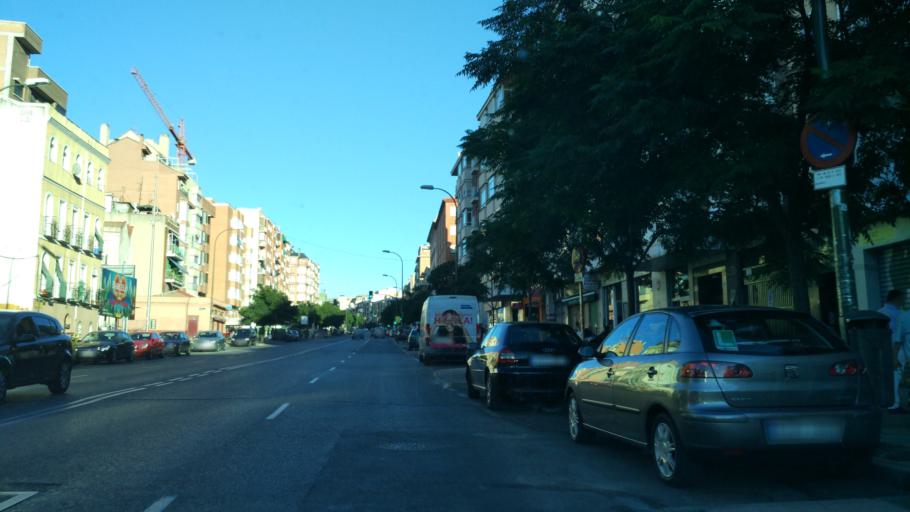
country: ES
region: Madrid
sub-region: Provincia de Madrid
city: Tetuan de las Victorias
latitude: 40.4630
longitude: -3.7031
